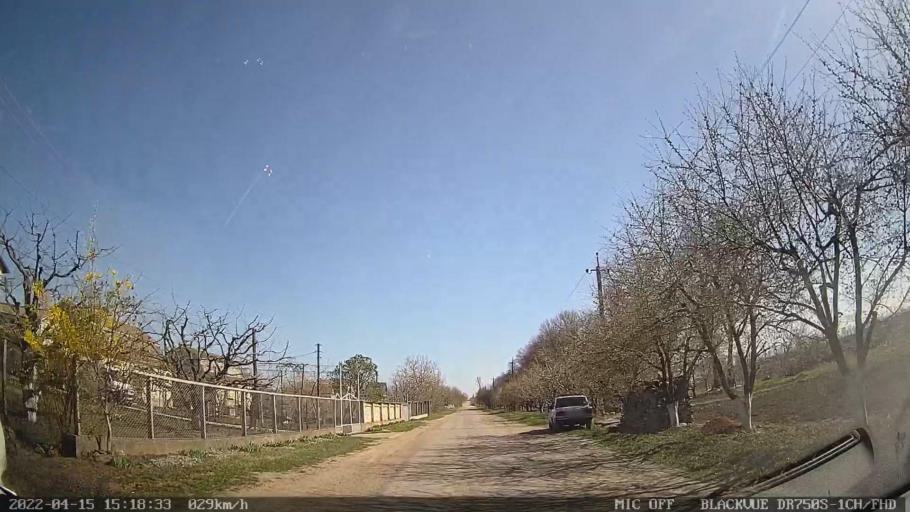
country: MD
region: Raionul Ocnita
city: Otaci
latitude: 48.3902
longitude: 27.9029
